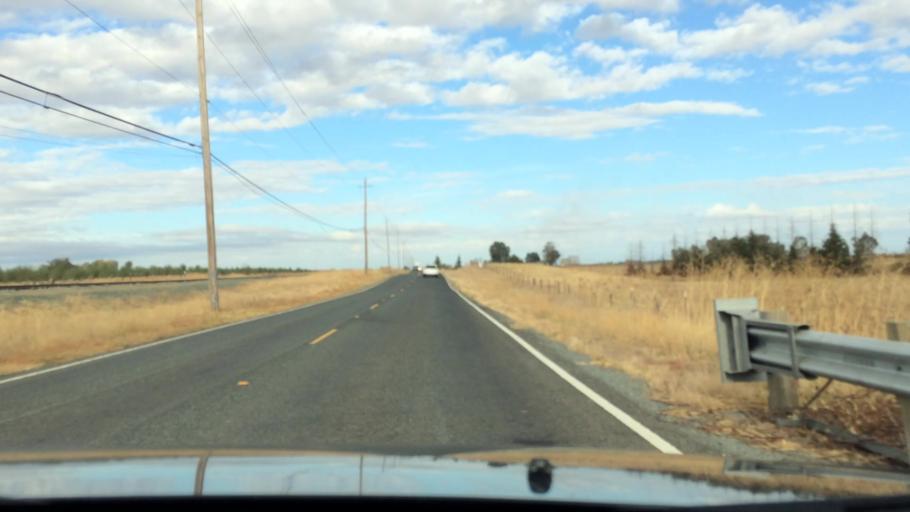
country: US
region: California
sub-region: Sacramento County
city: Herald
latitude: 38.3125
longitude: -121.2142
